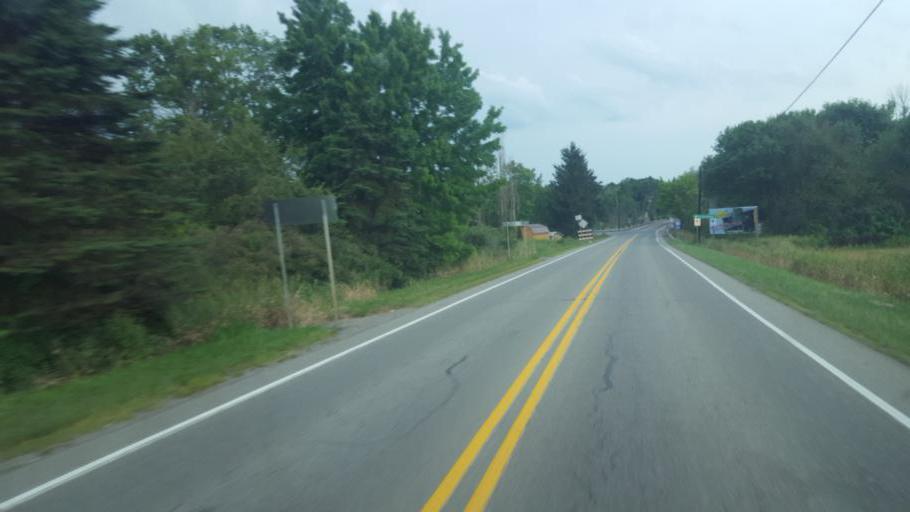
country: US
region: Pennsylvania
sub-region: Clarion County
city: Knox
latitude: 41.1928
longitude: -79.5474
